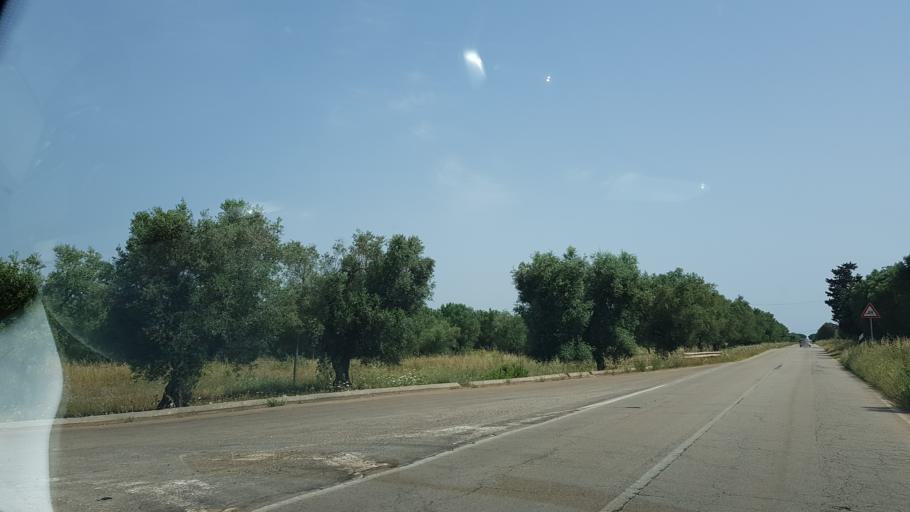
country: IT
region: Apulia
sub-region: Provincia di Brindisi
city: San Pancrazio Salentino
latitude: 40.3542
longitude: 17.8447
